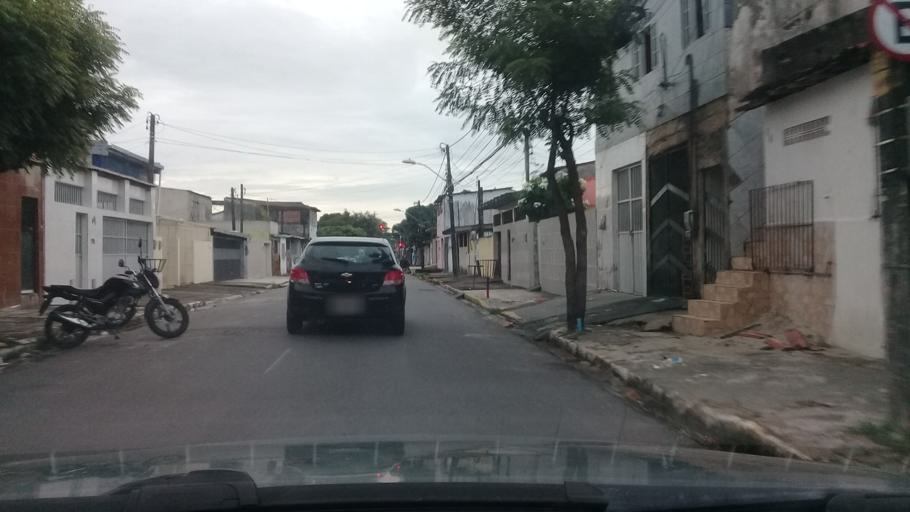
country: BR
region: Pernambuco
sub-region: Recife
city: Recife
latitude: -8.1092
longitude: -34.9255
